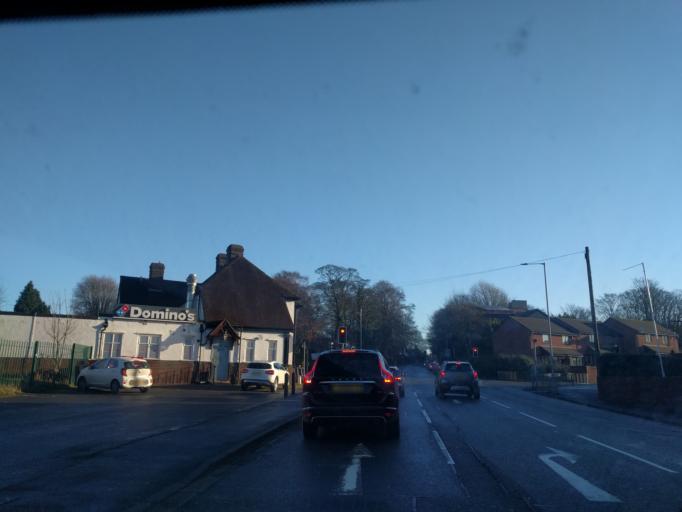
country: GB
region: England
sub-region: Telford and Wrekin
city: Wellington
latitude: 52.6964
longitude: -2.5011
